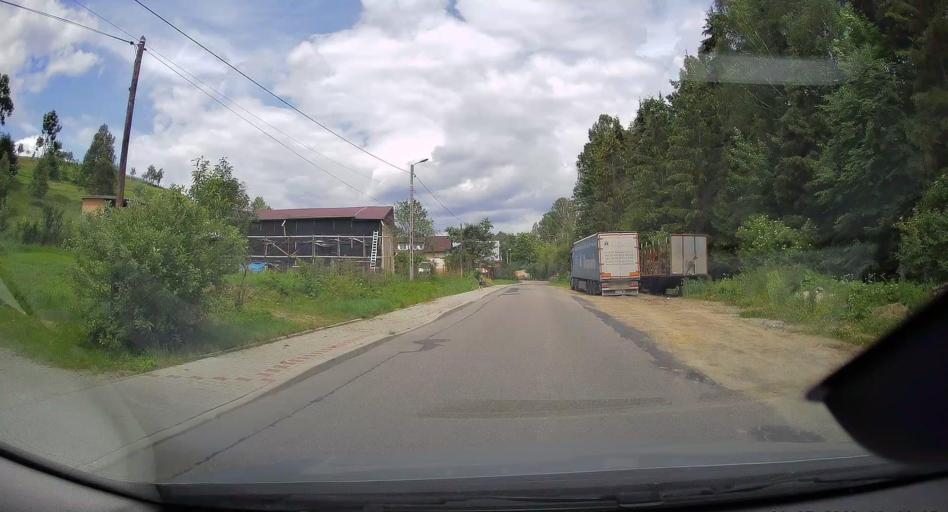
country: PL
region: Lesser Poland Voivodeship
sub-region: Powiat nowosadecki
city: Muszyna
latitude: 49.3793
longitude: 20.8936
